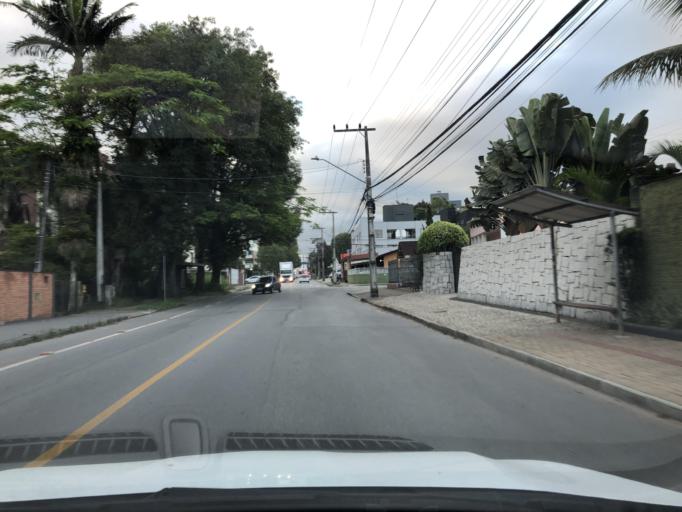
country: BR
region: Santa Catarina
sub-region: Joinville
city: Joinville
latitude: -26.2750
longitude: -48.8599
